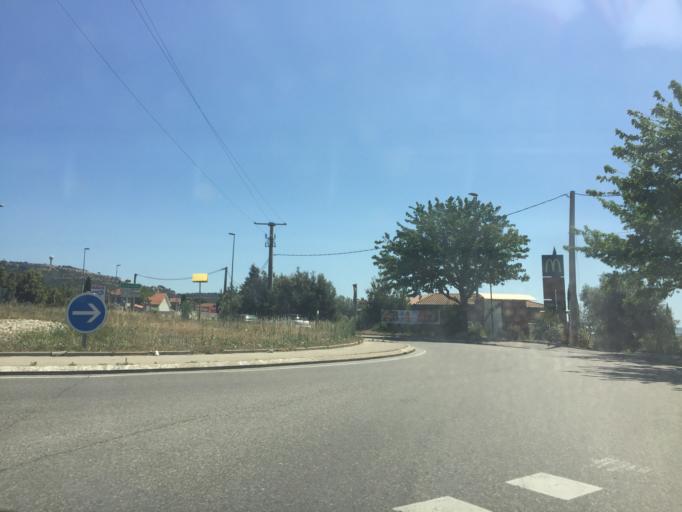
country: FR
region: Provence-Alpes-Cote d'Azur
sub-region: Departement des Bouches-du-Rhone
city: Rognac
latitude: 43.4855
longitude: 5.2226
